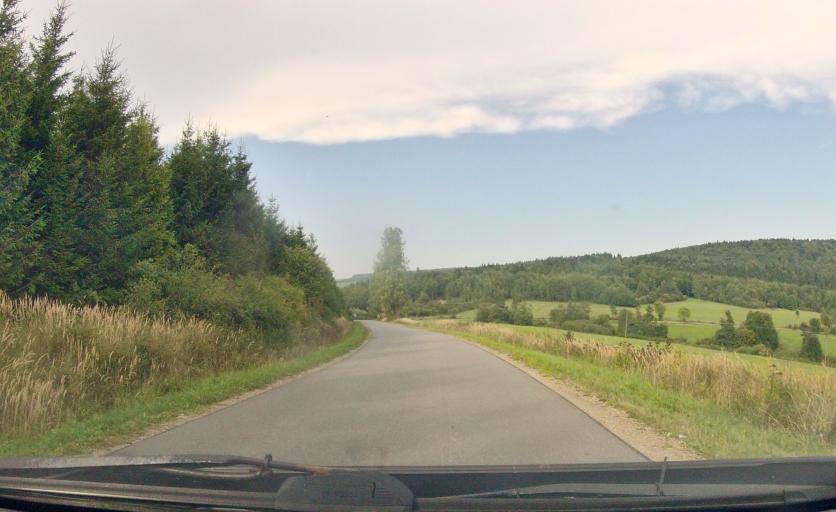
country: PL
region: Subcarpathian Voivodeship
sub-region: Powiat krosnienski
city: Dukla
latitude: 49.5084
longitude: 21.6275
